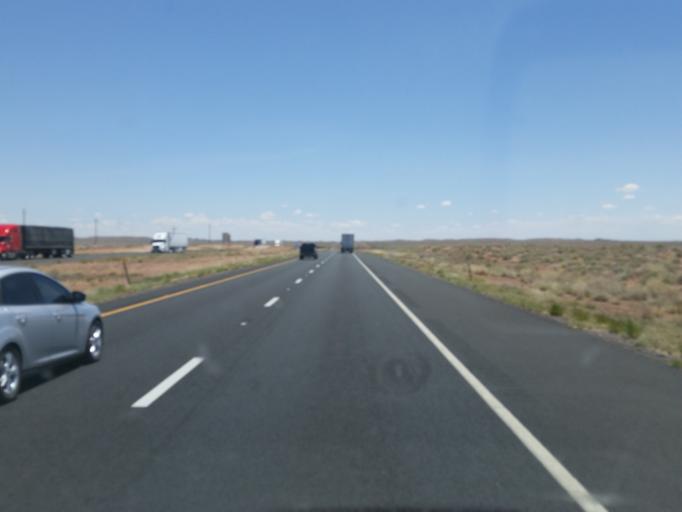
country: US
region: Arizona
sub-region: Coconino County
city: LeChee
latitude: 35.0574
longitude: -110.8019
